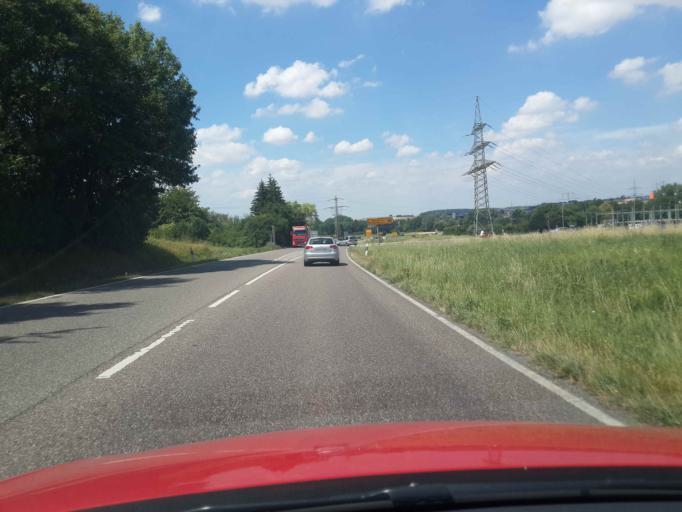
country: DE
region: Baden-Wuerttemberg
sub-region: Regierungsbezirk Stuttgart
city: Leingarten
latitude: 49.1416
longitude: 9.1453
